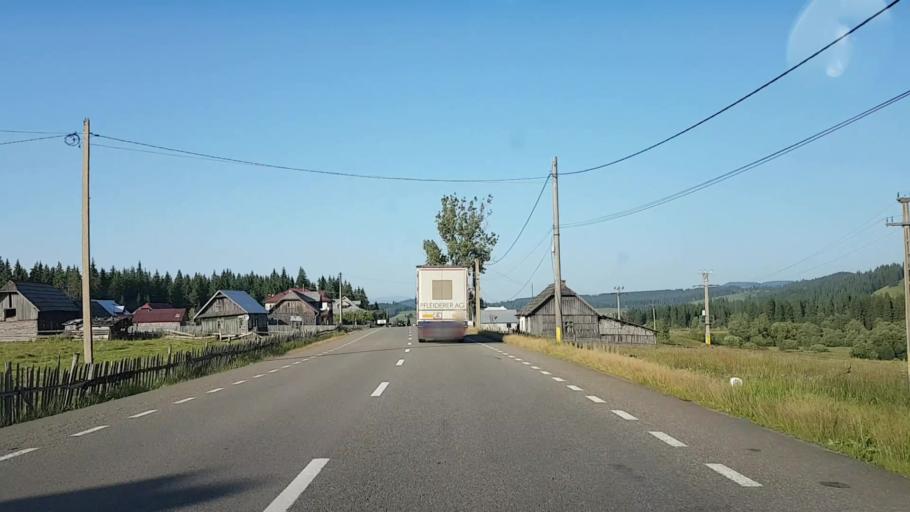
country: RO
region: Suceava
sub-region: Comuna Poiana Stampei
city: Poiana Stampei
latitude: 47.3044
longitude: 25.1163
